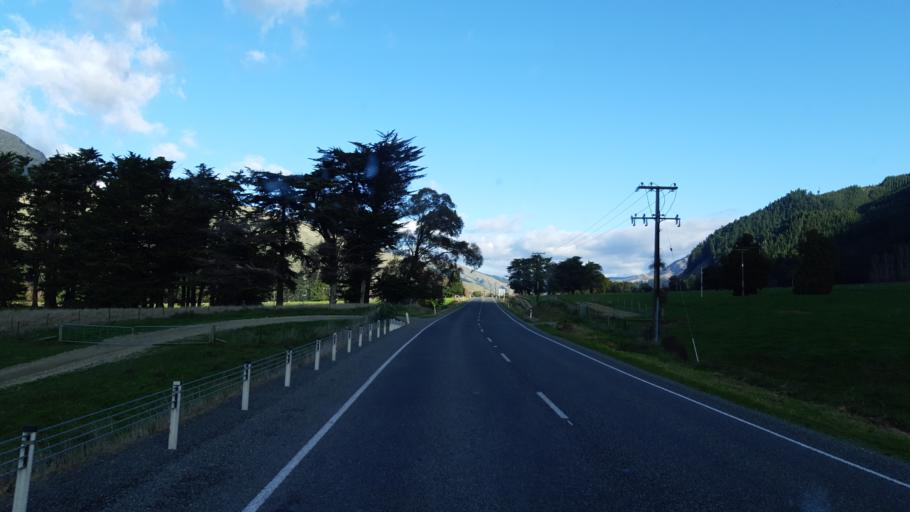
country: NZ
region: Marlborough
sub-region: Marlborough District
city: Picton
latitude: -41.2966
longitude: 173.7702
